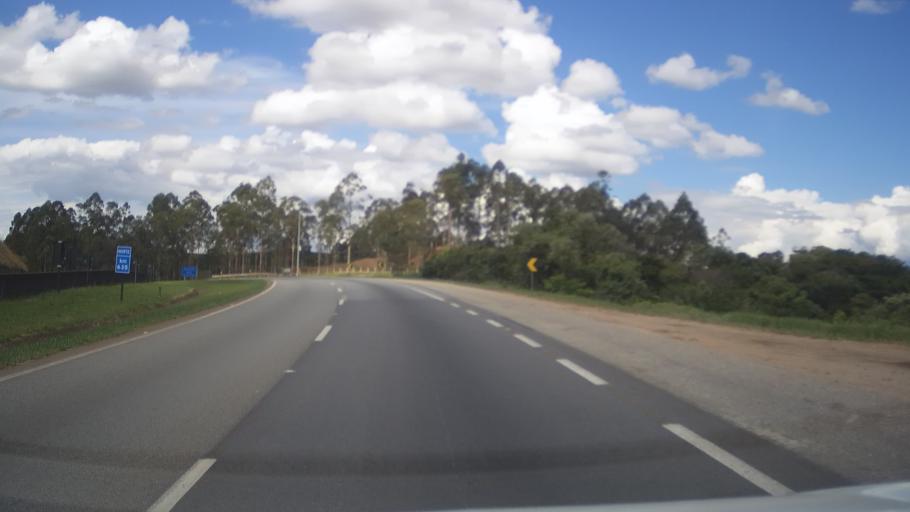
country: BR
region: Minas Gerais
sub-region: Santo Antonio Do Amparo
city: Santo Antonio do Amparo
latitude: -20.8601
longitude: -44.8376
